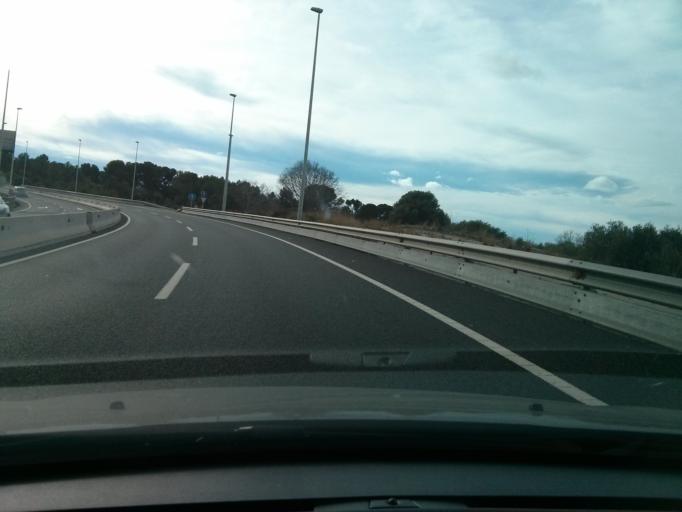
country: ES
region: Catalonia
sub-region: Provincia de Tarragona
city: Tarragona
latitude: 41.1376
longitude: 1.2379
